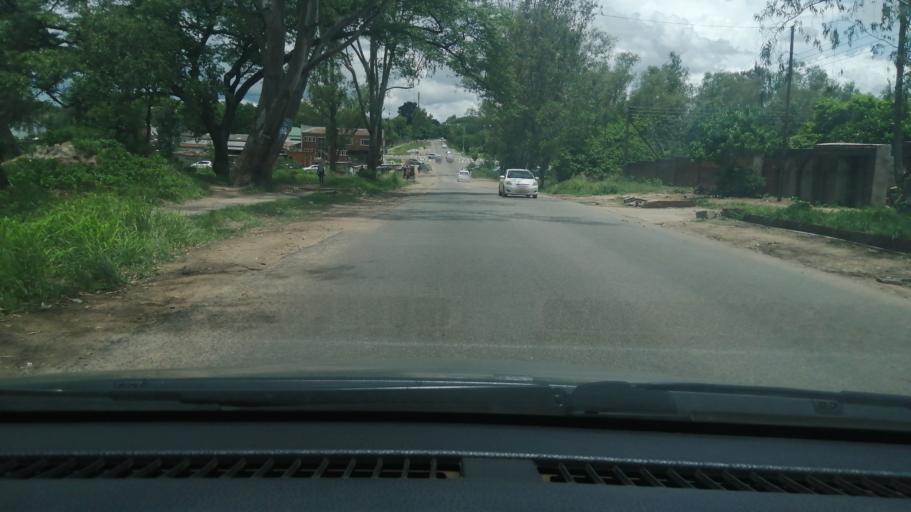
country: ZW
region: Harare
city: Harare
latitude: -17.8825
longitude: 31.0782
